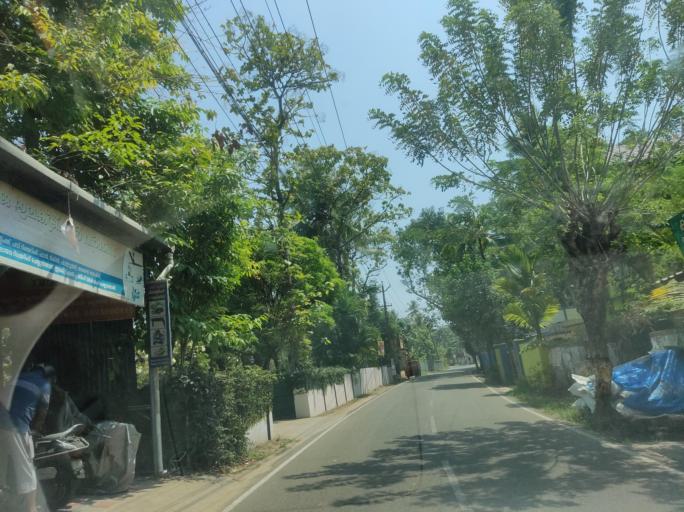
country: IN
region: Kerala
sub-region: Alappuzha
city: Kutiatodu
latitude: 9.8050
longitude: 76.3011
